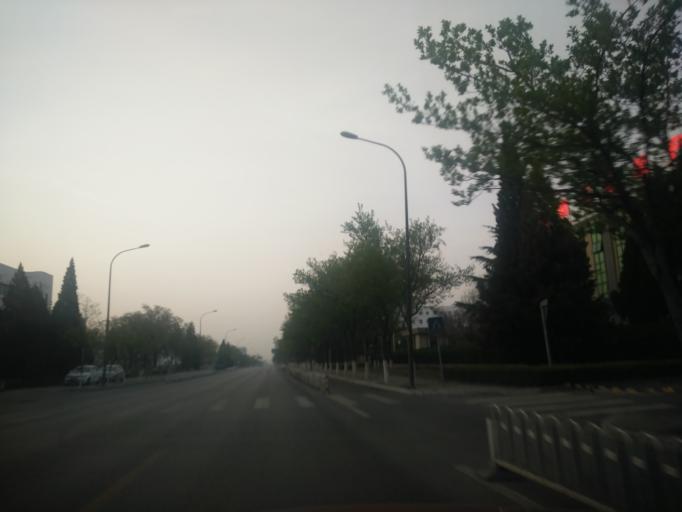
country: CN
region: Beijing
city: Jiugong
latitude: 39.8006
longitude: 116.5063
